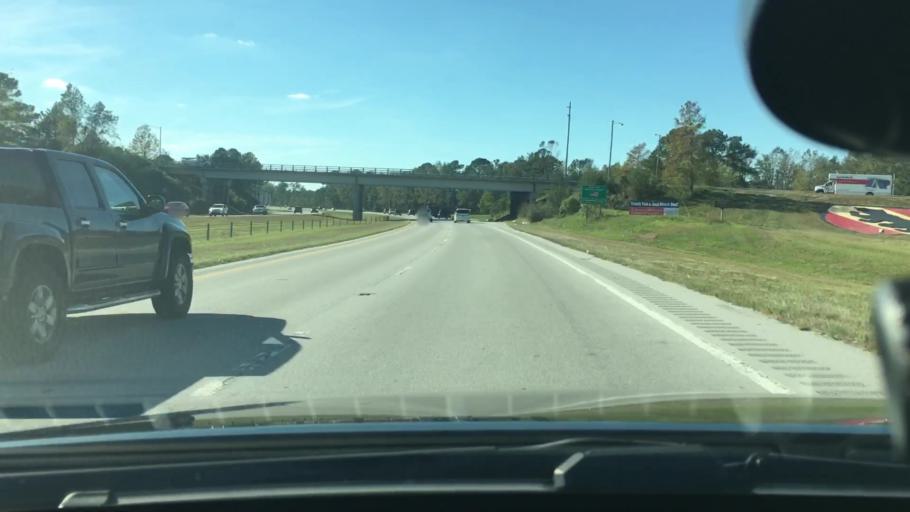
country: US
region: North Carolina
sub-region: Craven County
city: New Bern
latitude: 35.1008
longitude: -77.0570
